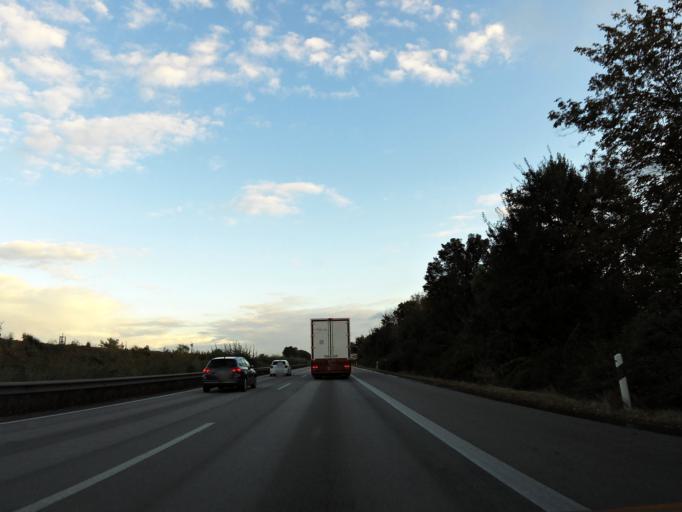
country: DE
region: Rheinland-Pfalz
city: Zotzenheim
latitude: 49.8599
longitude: 7.9701
